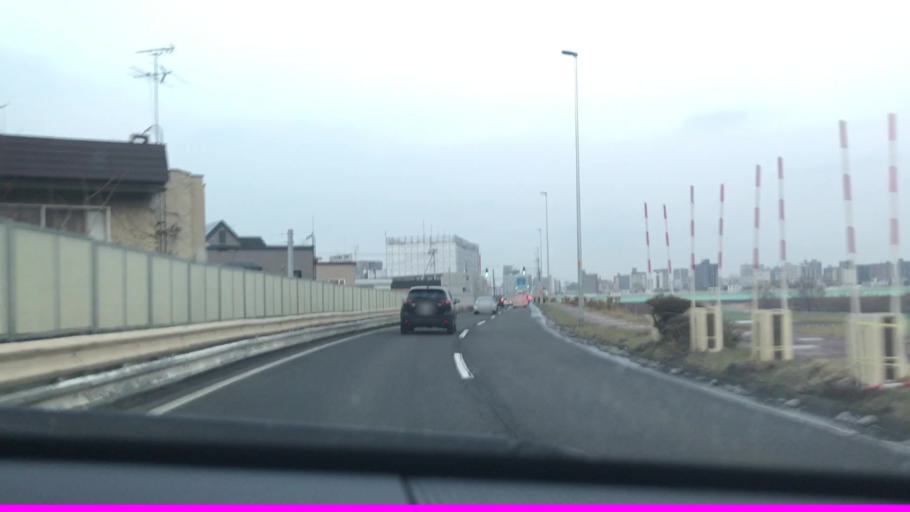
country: JP
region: Hokkaido
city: Sapporo
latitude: 43.0274
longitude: 141.3515
